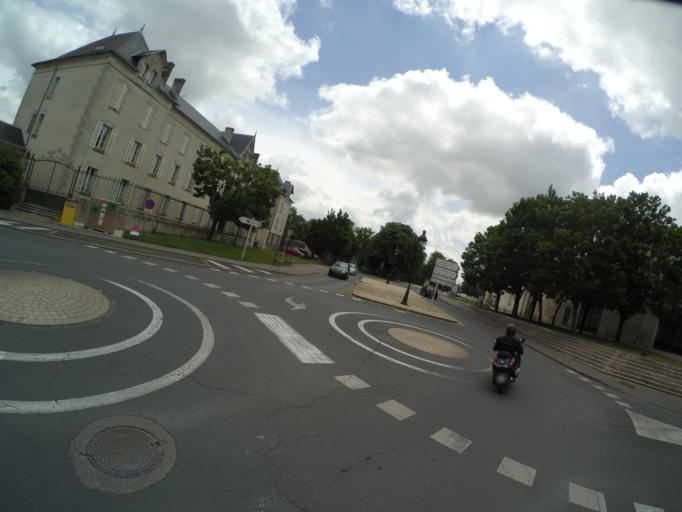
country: FR
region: Poitou-Charentes
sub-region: Departement de la Charente-Maritime
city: Rochefort
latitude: 45.9409
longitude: -0.9584
